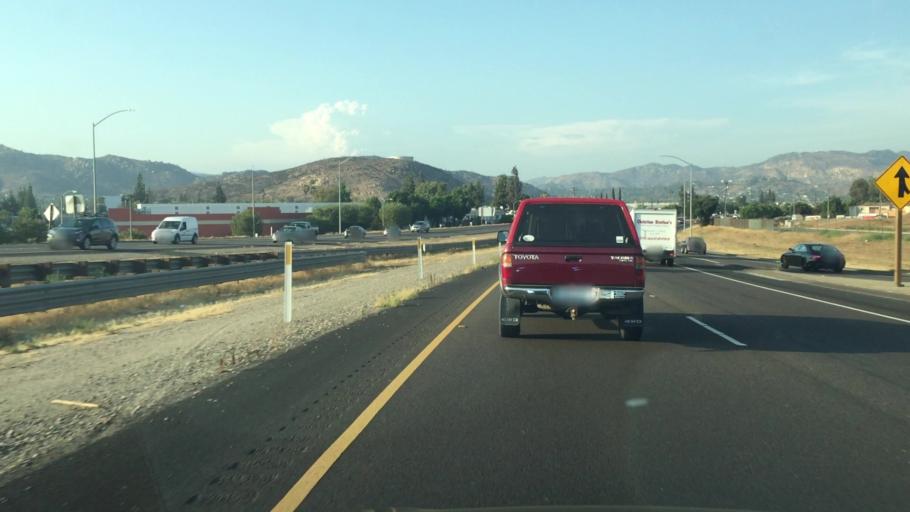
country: US
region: California
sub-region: San Diego County
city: Santee
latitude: 32.8426
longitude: -116.9608
